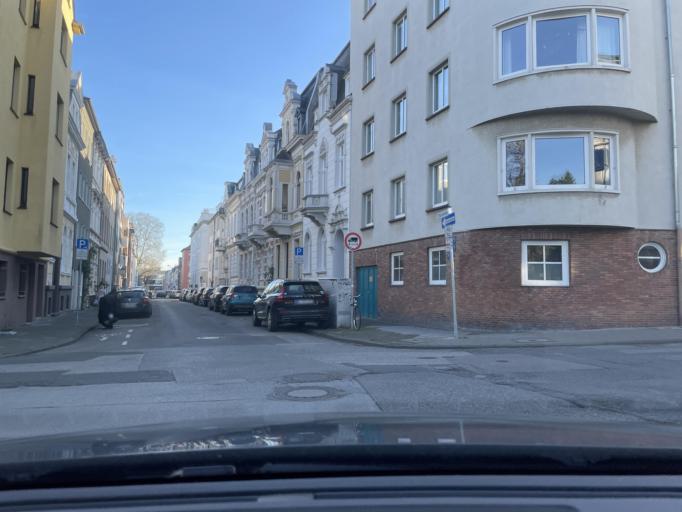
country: DE
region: North Rhine-Westphalia
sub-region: Regierungsbezirk Dusseldorf
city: Monchengladbach
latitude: 51.1988
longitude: 6.4346
